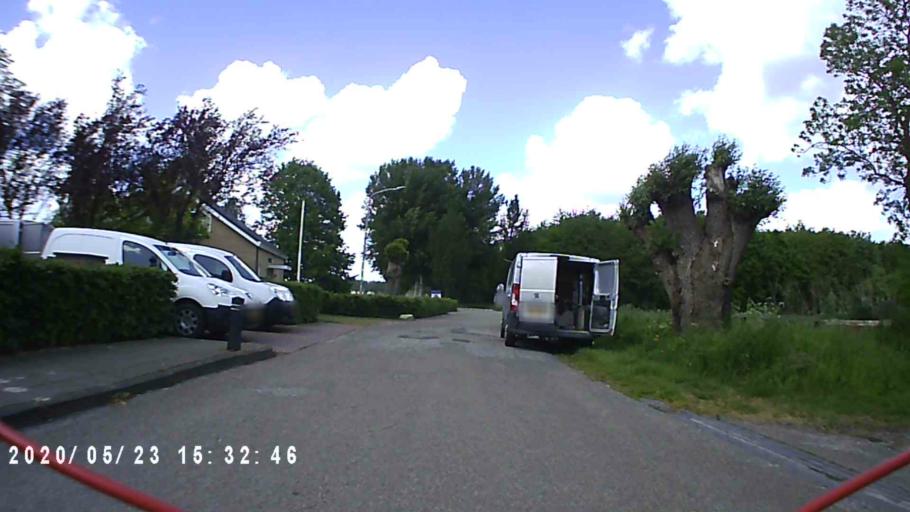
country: NL
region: Groningen
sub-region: Gemeente Delfzijl
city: Delfzijl
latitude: 53.2596
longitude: 6.9363
